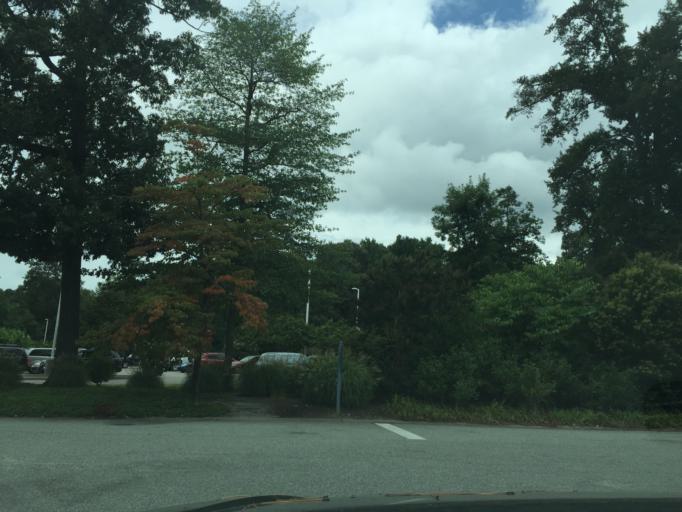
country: US
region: Virginia
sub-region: City of Newport News
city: Newport News
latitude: 37.0554
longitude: -76.4885
